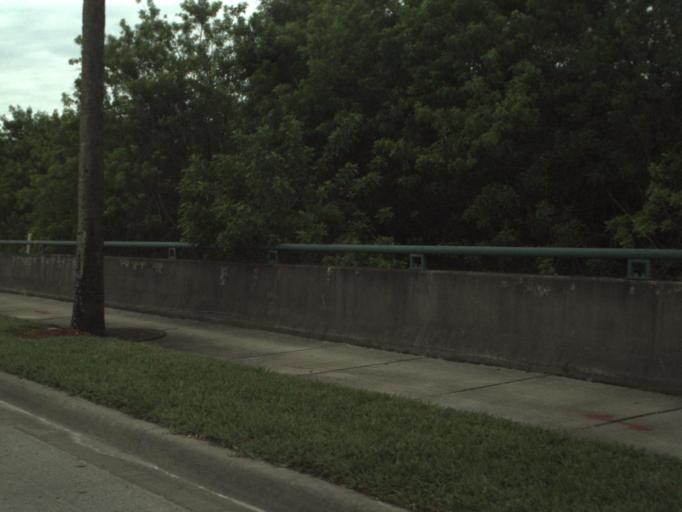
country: US
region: Florida
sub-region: Palm Beach County
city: Wellington
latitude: 26.6814
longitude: -80.2419
